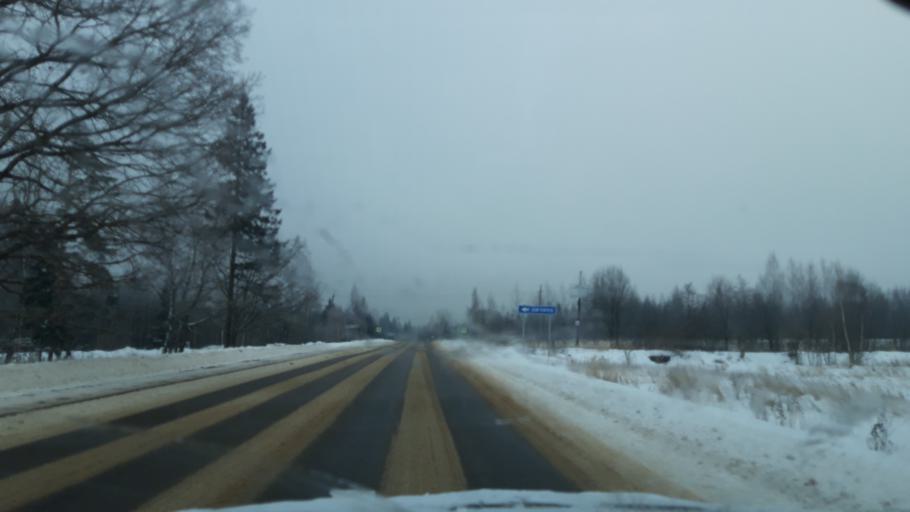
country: RU
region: Moskovskaya
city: Avtopoligon
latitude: 56.2651
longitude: 37.2641
